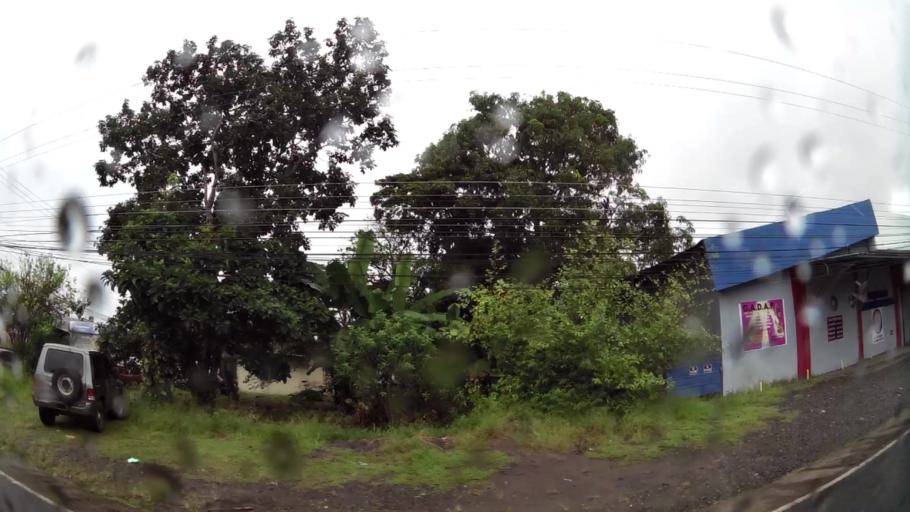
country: PA
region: Chiriqui
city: David
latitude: 8.4308
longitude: -82.4353
